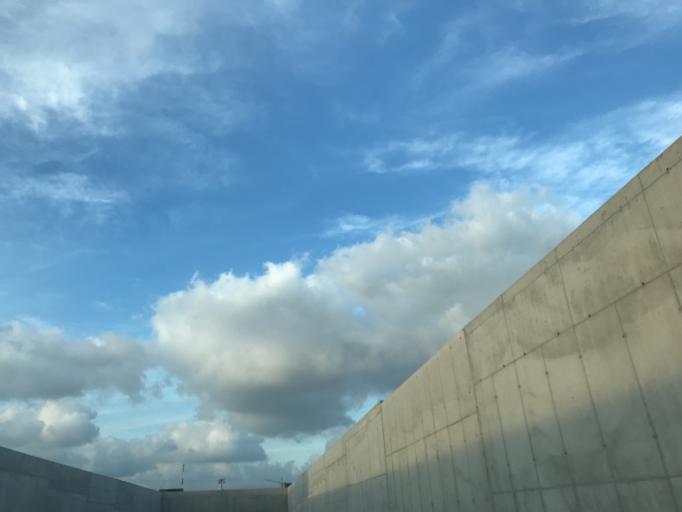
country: TR
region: Istanbul
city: Durusu
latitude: 41.2626
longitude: 28.7143
